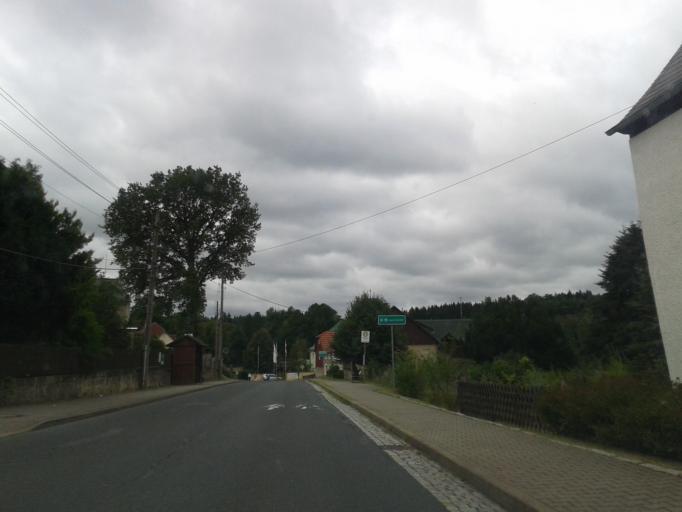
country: DE
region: Saxony
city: Dorfhain
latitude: 50.9540
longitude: 13.5084
